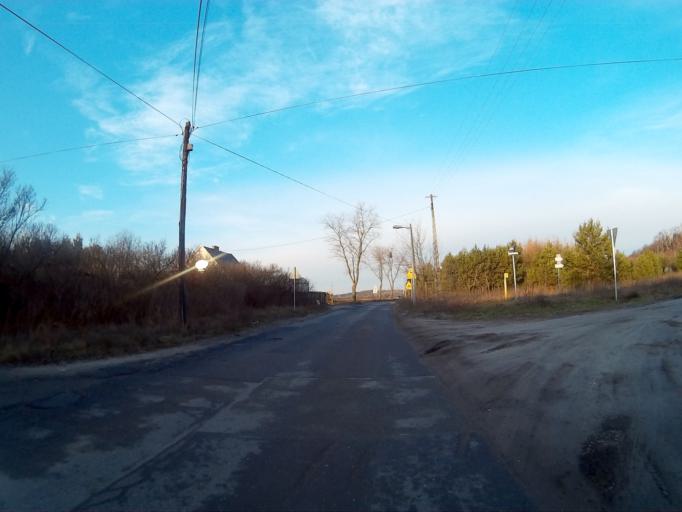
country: PL
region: Kujawsko-Pomorskie
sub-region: Powiat bydgoski
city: Osielsko
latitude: 53.1581
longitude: 18.0984
